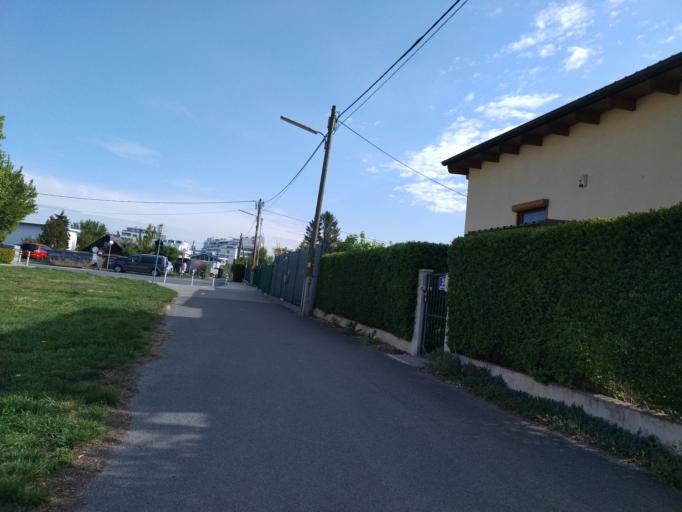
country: AT
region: Lower Austria
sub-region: Politischer Bezirk Modling
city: Vosendorf
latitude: 48.1577
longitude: 16.3164
